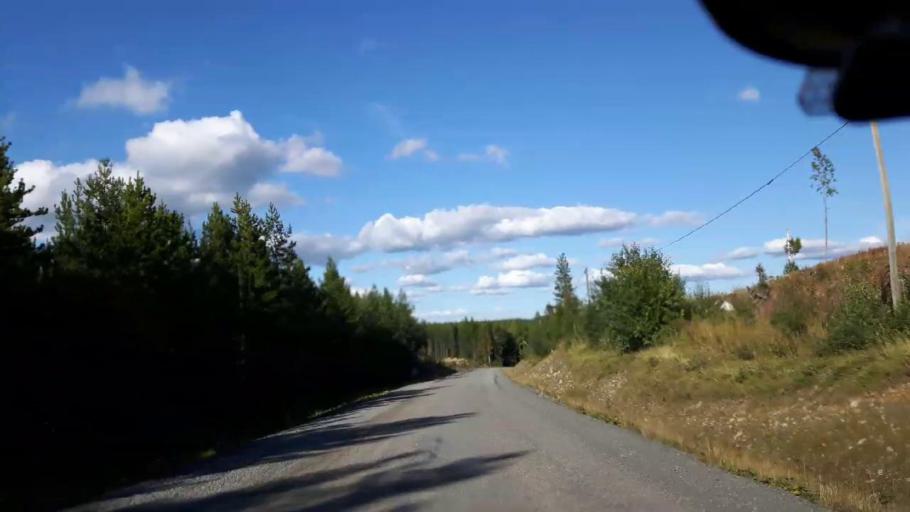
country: SE
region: Jaemtland
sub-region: Ragunda Kommun
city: Hammarstrand
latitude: 63.4519
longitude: 16.2285
